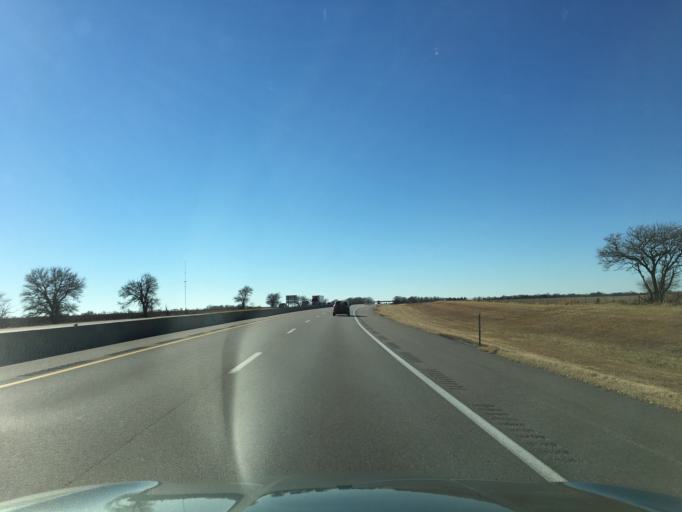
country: US
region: Kansas
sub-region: Sumner County
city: Belle Plaine
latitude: 37.3417
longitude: -97.3242
